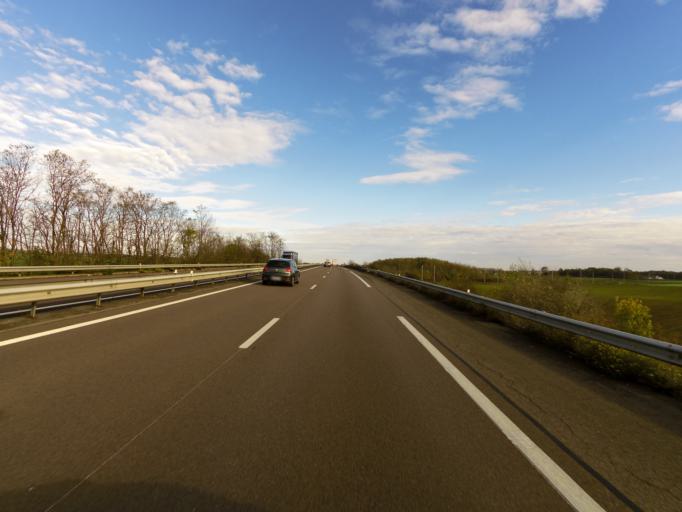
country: FR
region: Bourgogne
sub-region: Departement de la Cote-d'Or
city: Ouges
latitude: 47.2427
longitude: 5.0834
